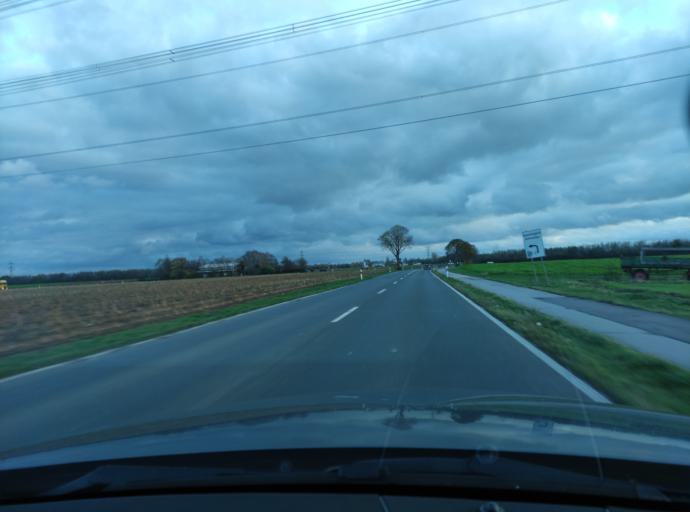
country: DE
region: North Rhine-Westphalia
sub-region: Regierungsbezirk Dusseldorf
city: Dormagen
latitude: 51.1108
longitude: 6.7796
